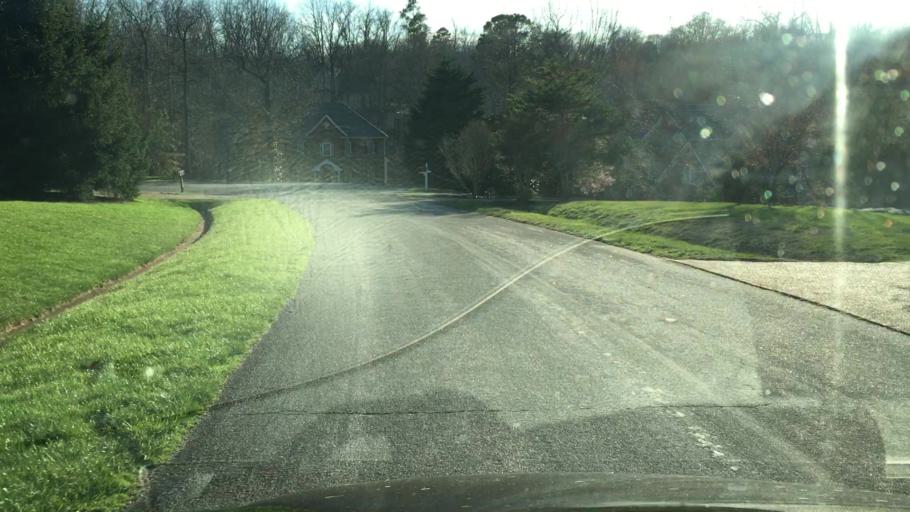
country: US
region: Virginia
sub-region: Chesterfield County
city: Bon Air
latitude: 37.5354
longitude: -77.6106
